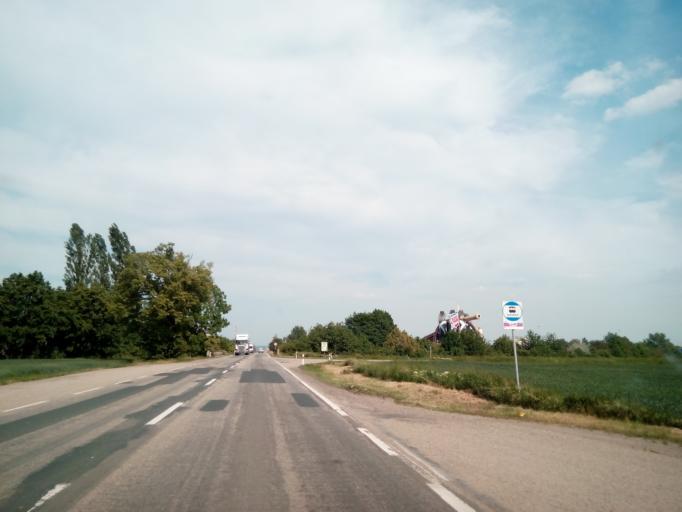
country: CZ
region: South Moravian
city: Blazovice
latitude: 49.1845
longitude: 16.7992
